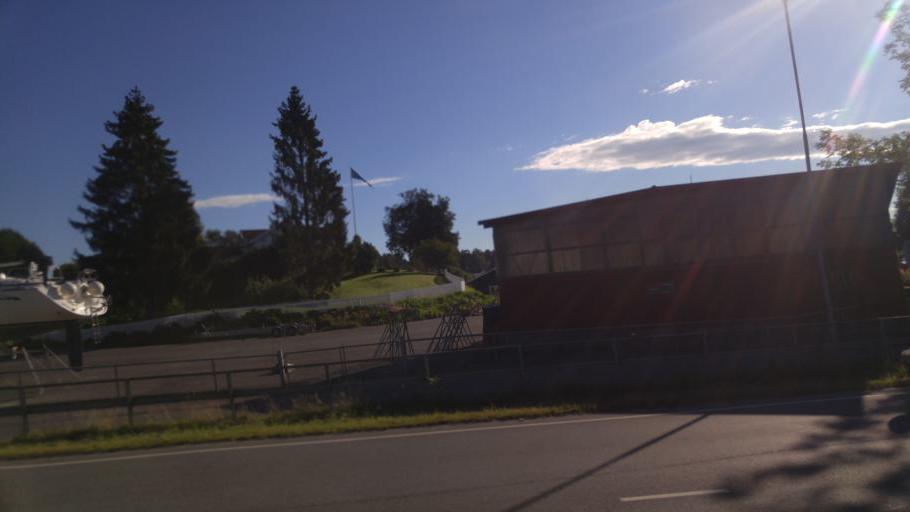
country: NO
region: Akershus
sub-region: Asker
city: Billingstad
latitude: 59.8555
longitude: 10.4918
